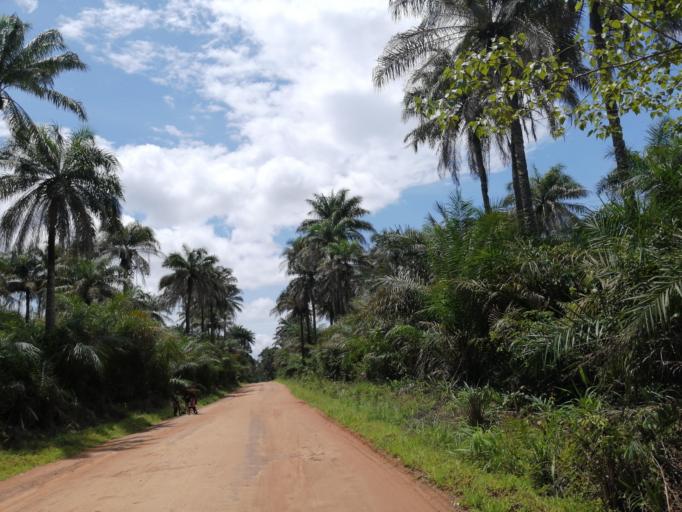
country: SL
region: Northern Province
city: Konakridee
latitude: 8.7682
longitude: -13.1402
